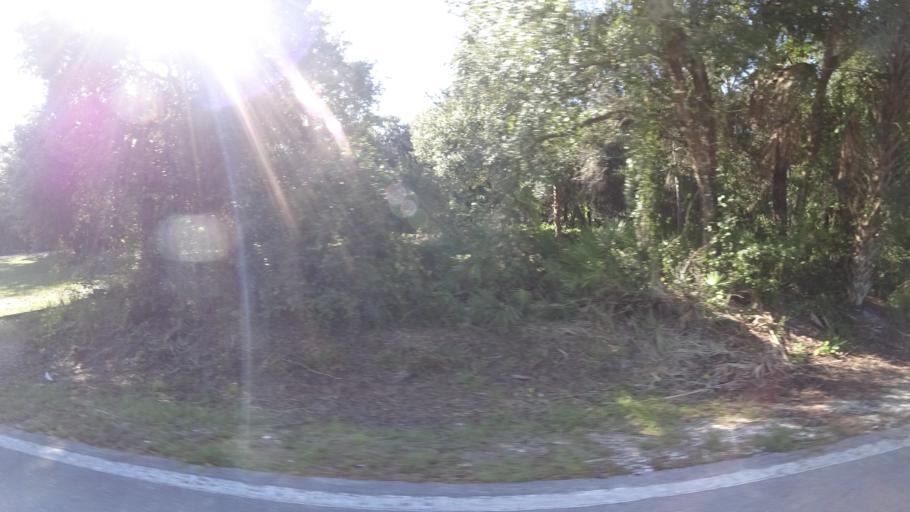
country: US
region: Florida
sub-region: Sarasota County
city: The Meadows
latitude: 27.4136
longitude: -82.4487
